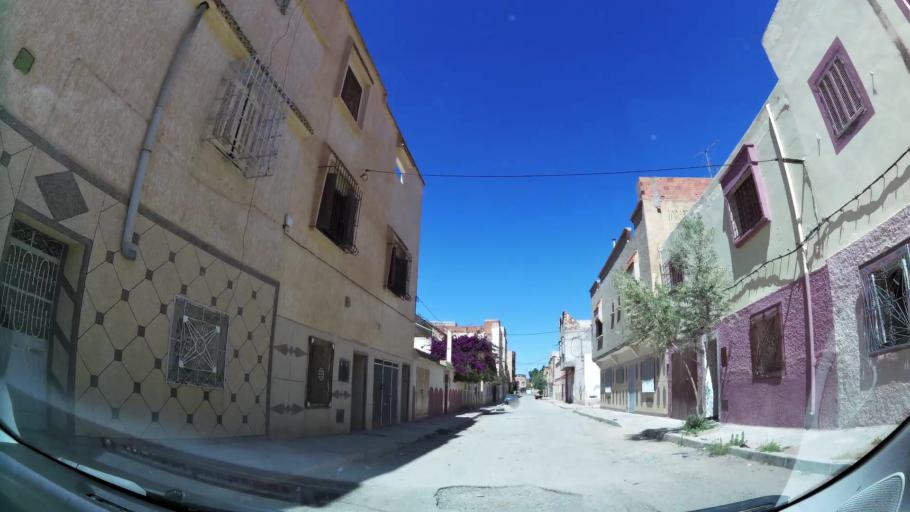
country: MA
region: Oriental
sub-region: Oujda-Angad
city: Oujda
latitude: 34.6664
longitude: -1.8731
